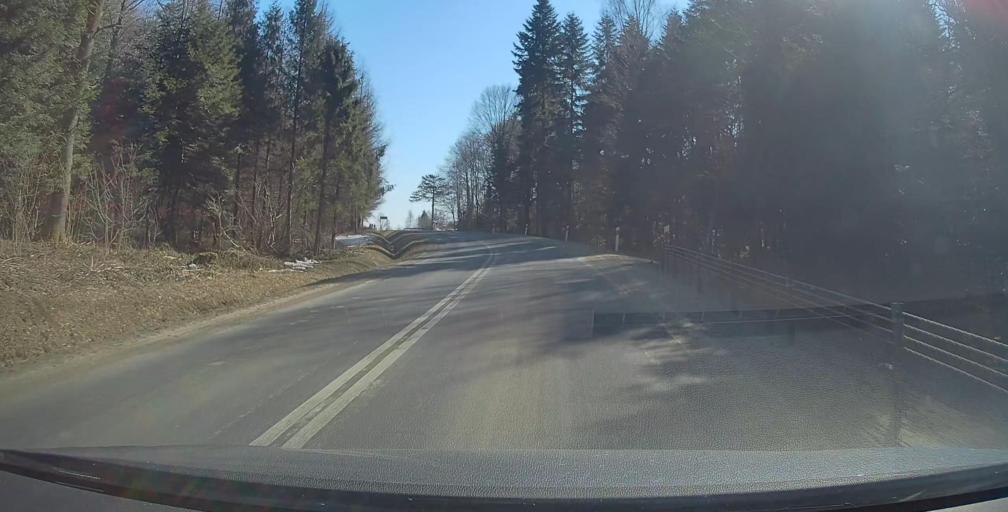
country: PL
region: Subcarpathian Voivodeship
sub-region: Powiat bieszczadzki
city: Ustrzyki Dolne
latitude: 49.5193
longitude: 22.6049
